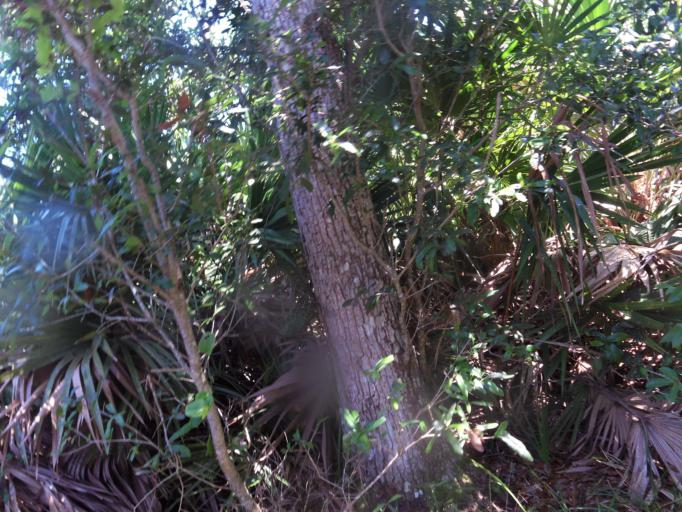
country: US
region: Florida
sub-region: Flagler County
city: Palm Coast
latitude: 29.6354
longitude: -81.2069
